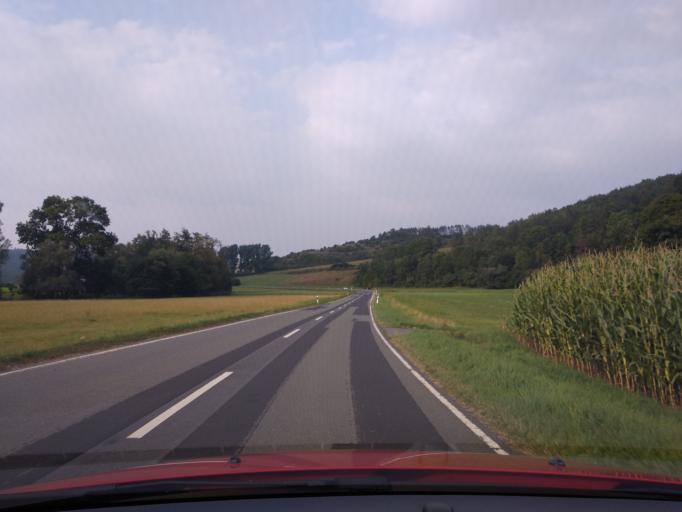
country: DE
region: Hesse
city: Liebenau
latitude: 51.4907
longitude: 9.2983
